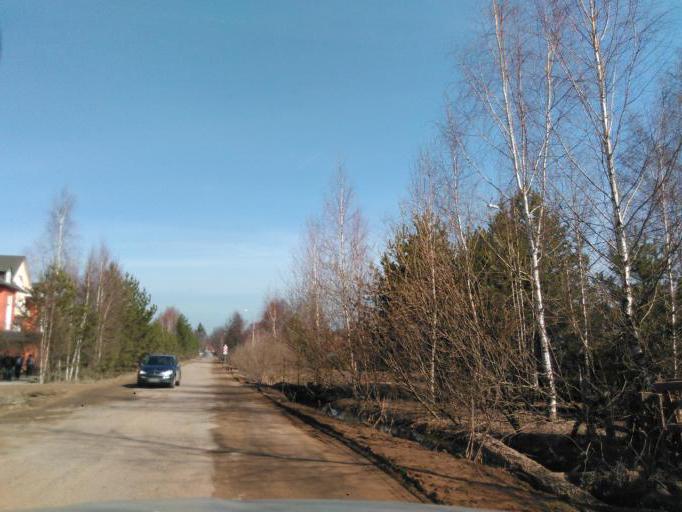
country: RU
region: Moskovskaya
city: Opalikha
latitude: 55.8838
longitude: 37.2640
